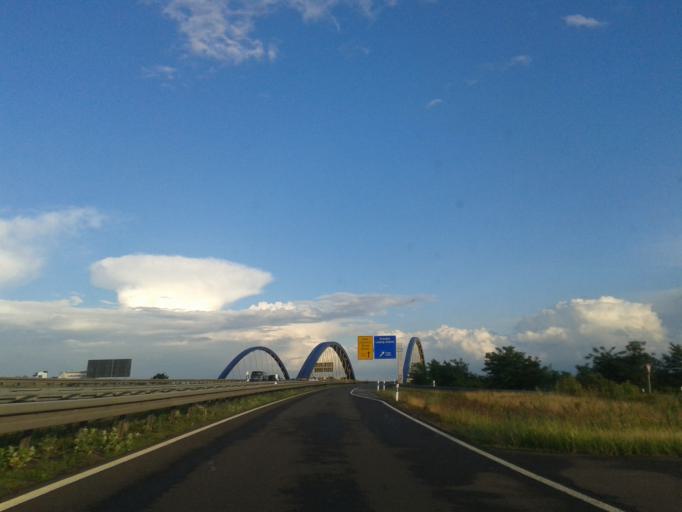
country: DE
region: Saxony
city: Markkleeberg
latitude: 51.2499
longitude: 12.3907
